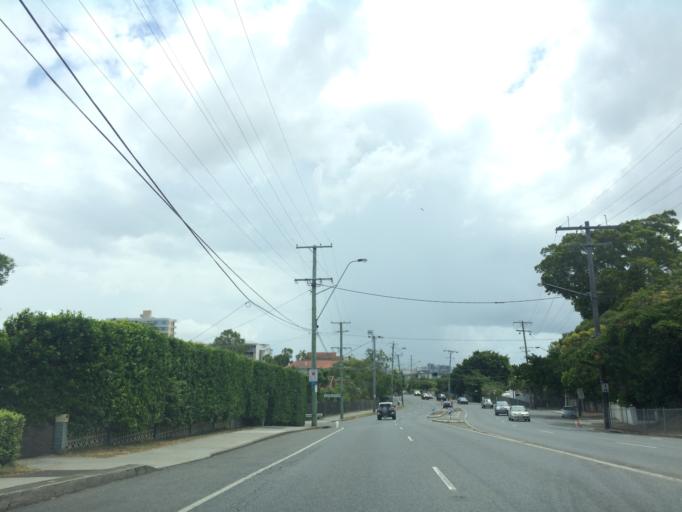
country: AU
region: Queensland
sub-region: Brisbane
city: Balmoral
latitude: -27.4729
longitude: 153.0586
